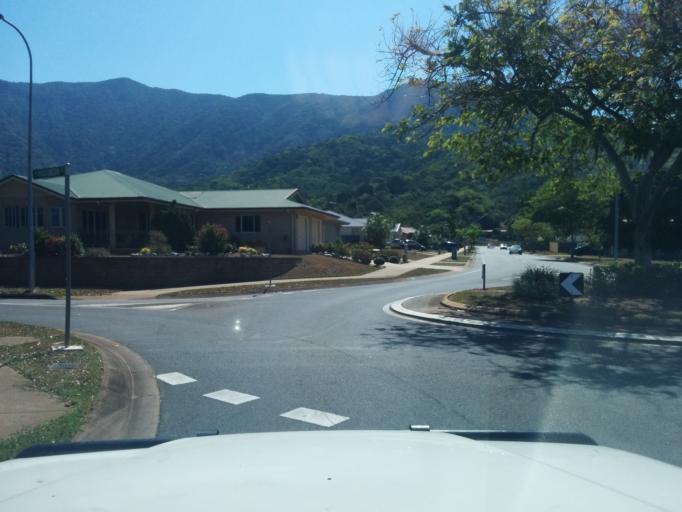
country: AU
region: Queensland
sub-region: Cairns
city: Redlynch
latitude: -16.8948
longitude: 145.6969
